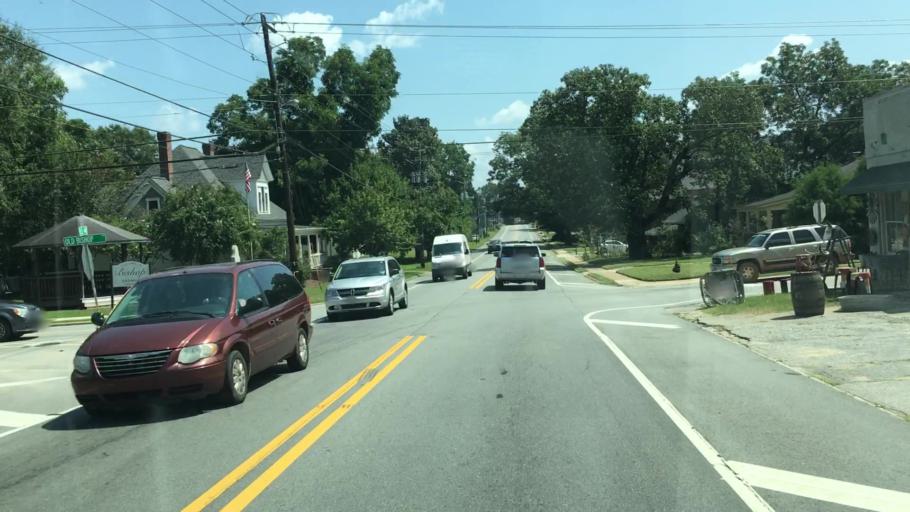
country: US
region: Georgia
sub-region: Oconee County
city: Watkinsville
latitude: 33.8199
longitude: -83.4393
